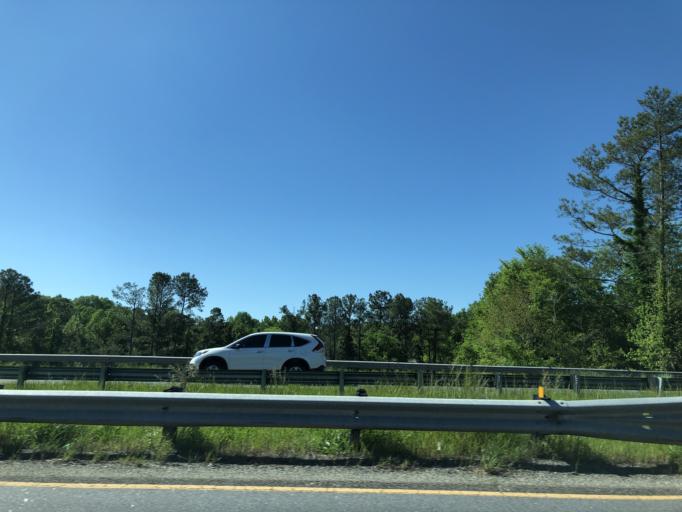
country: US
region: Georgia
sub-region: Clarke County
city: Country Club Estates
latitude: 33.9640
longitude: -83.4283
